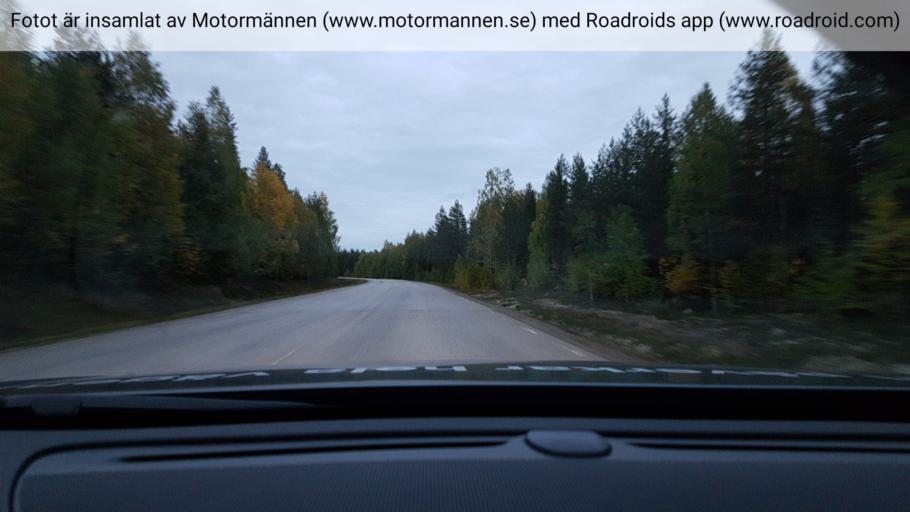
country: SE
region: Norrbotten
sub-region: Alvsbyns Kommun
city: AElvsbyn
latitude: 65.8513
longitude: 20.4486
